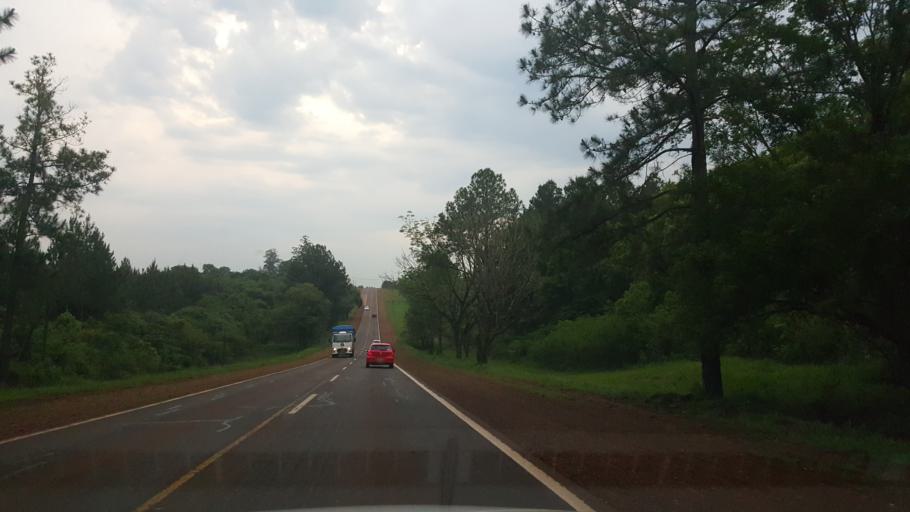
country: AR
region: Misiones
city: Santo Pipo
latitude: -27.1338
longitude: -55.3947
